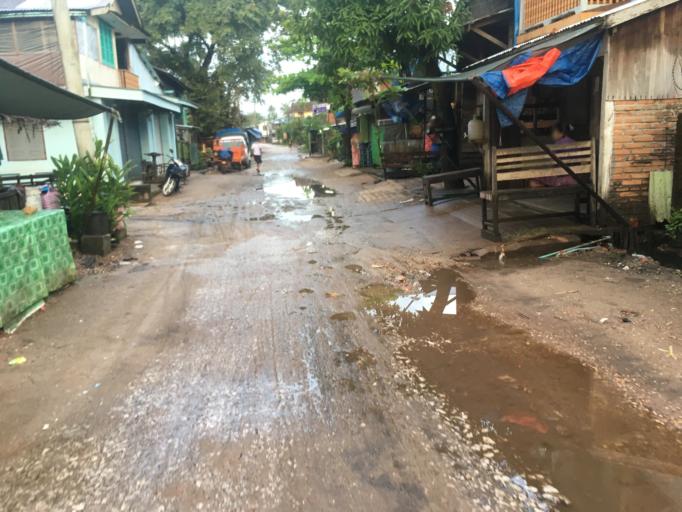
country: MM
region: Mon
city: Mawlamyine
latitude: 16.4641
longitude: 97.6260
